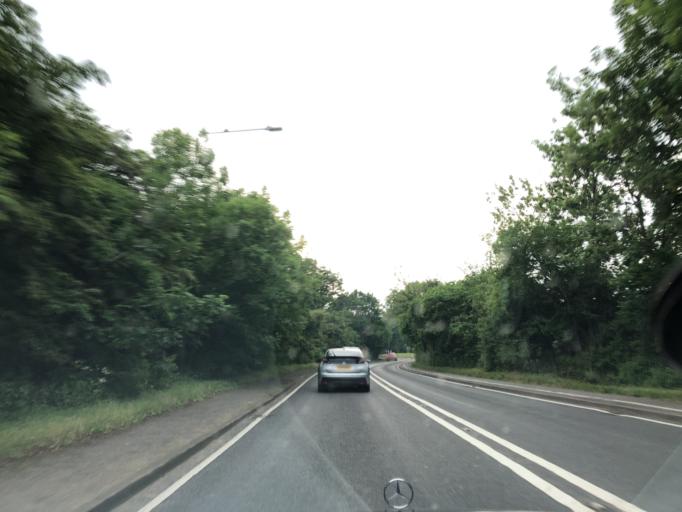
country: GB
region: England
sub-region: Warwickshire
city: Warwick
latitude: 52.2959
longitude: -1.6295
